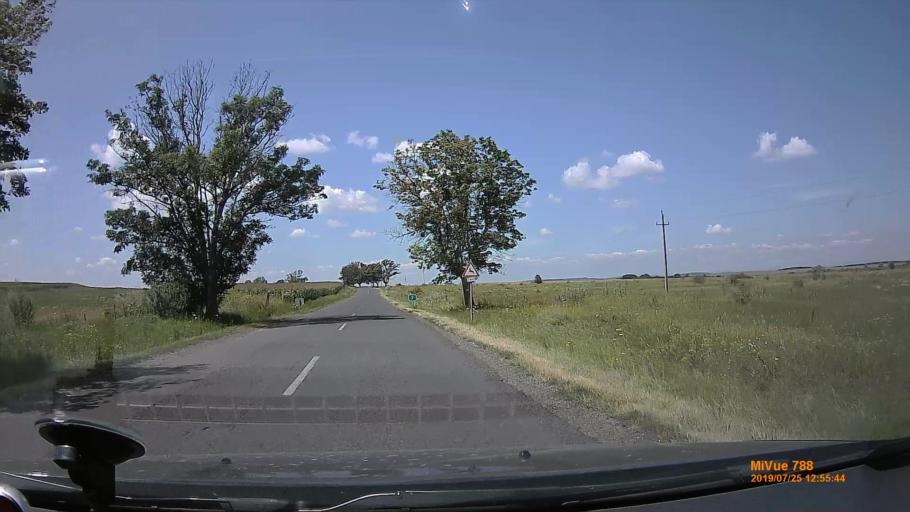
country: HU
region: Borsod-Abauj-Zemplen
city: Abaujszanto
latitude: 48.3113
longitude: 21.1835
